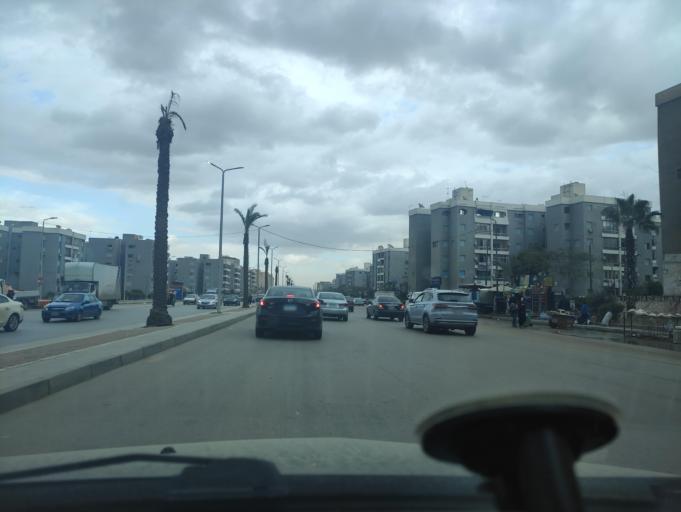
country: EG
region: Muhafazat al Qahirah
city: Cairo
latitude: 30.0500
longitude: 31.3884
